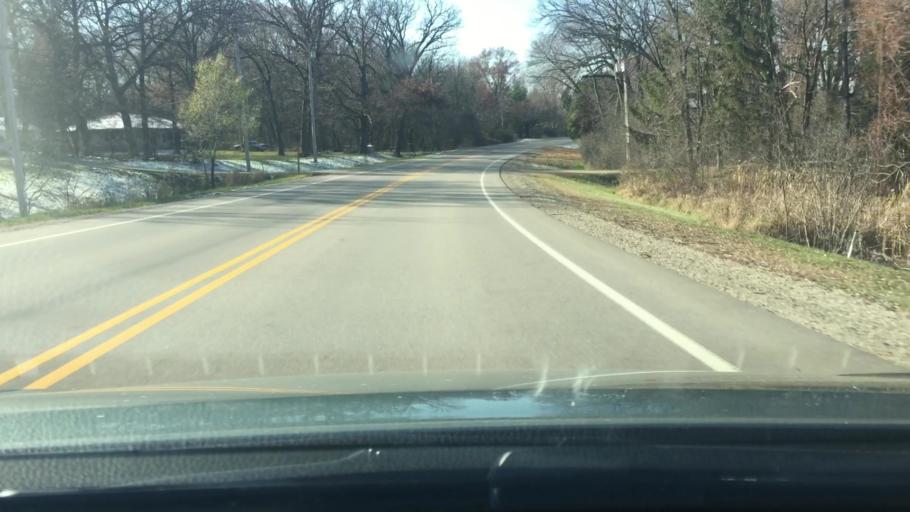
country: US
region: Wisconsin
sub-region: Jefferson County
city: Cambridge
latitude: 43.0093
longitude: -89.0029
